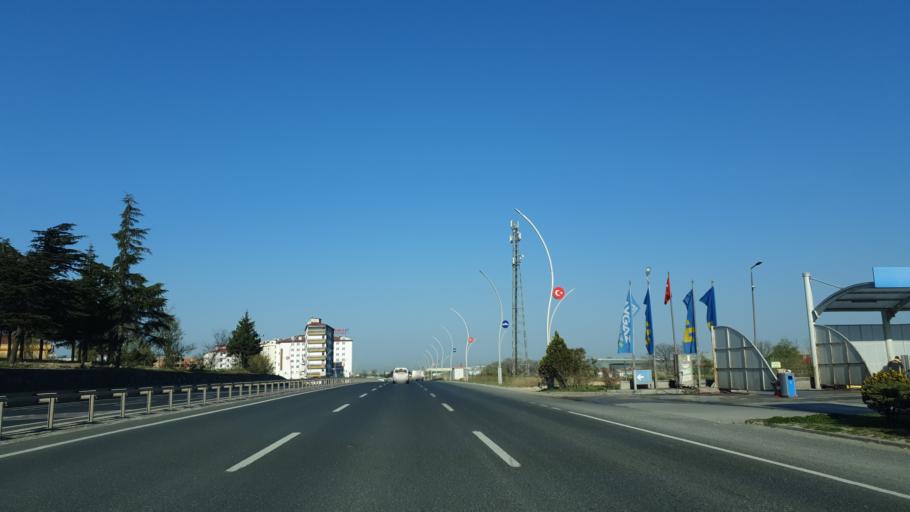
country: TR
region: Tekirdag
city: Cerkezkoey
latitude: 41.2732
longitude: 27.9734
